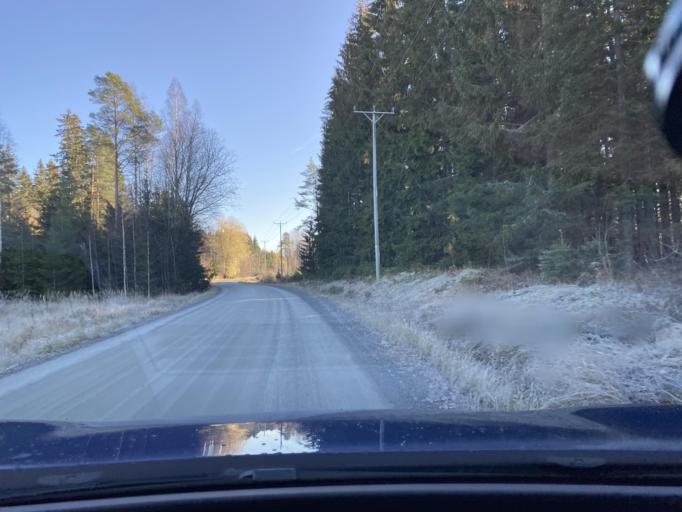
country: FI
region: Pirkanmaa
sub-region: Etelae-Pirkanmaa
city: Toijala
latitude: 61.0257
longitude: 23.8235
